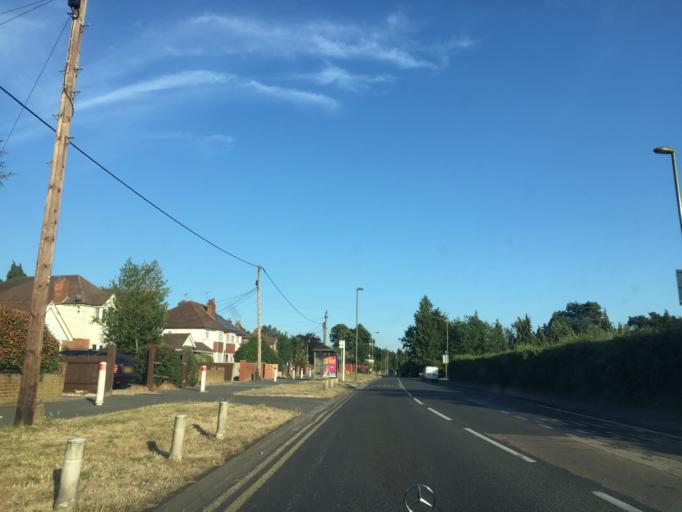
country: GB
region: England
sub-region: Surrey
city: Frimley
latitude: 51.3082
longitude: -0.7321
